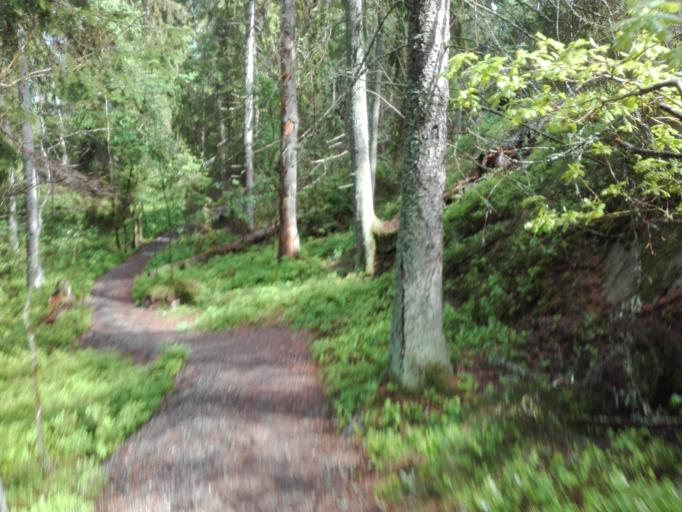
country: SE
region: Stockholm
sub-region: Nacka Kommun
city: Fisksatra
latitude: 59.2955
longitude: 18.2720
